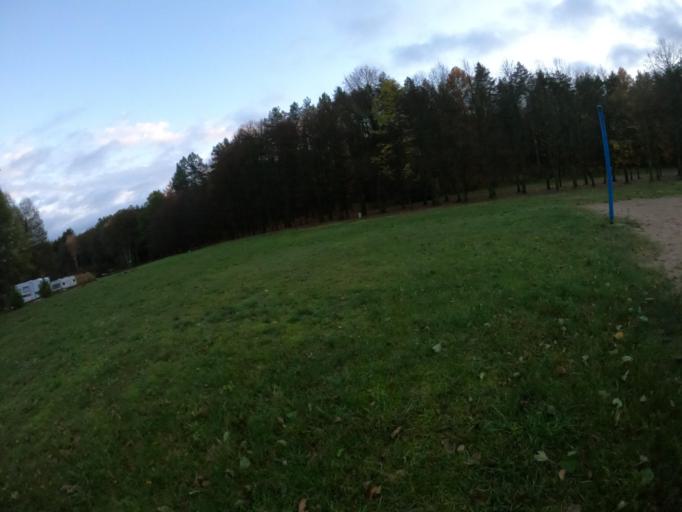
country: PL
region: West Pomeranian Voivodeship
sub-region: Powiat walecki
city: Tuczno
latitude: 53.1844
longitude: 16.1701
